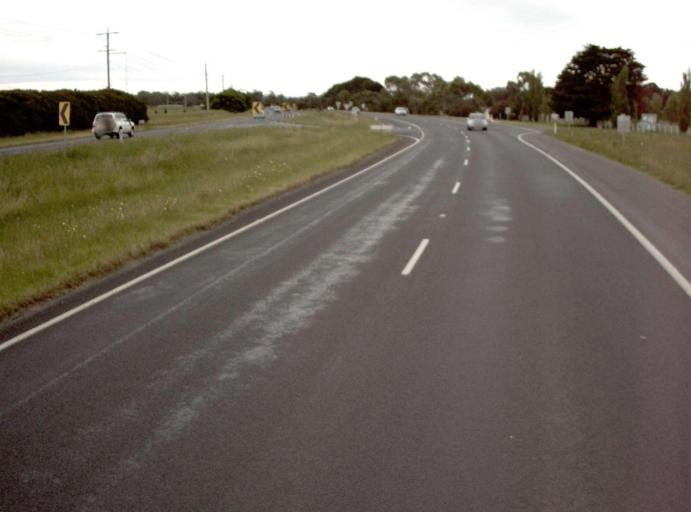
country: AU
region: Victoria
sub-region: Cardinia
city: Koo-Wee-Rup
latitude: -38.2238
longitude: 145.5096
